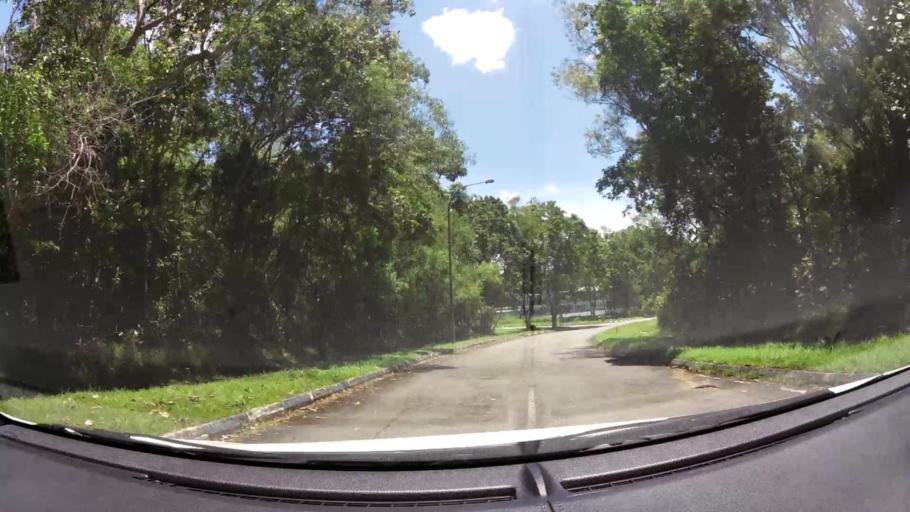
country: BN
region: Brunei and Muara
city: Bandar Seri Begawan
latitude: 4.9198
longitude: 114.9581
